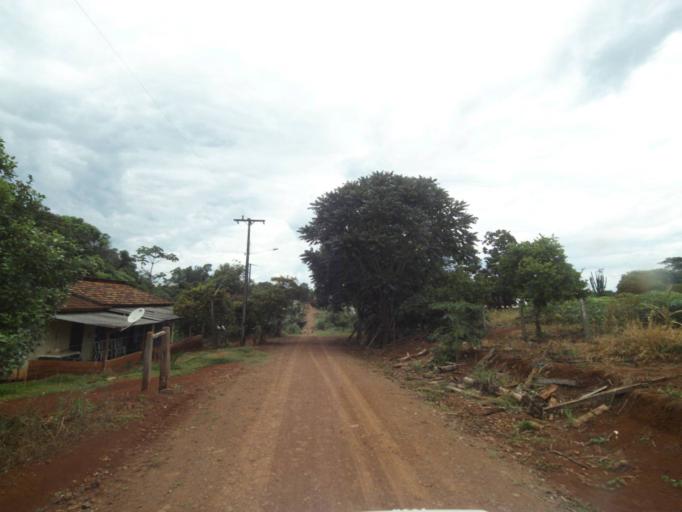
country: BR
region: Parana
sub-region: Guaraniacu
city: Guaraniacu
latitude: -24.9173
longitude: -52.9359
